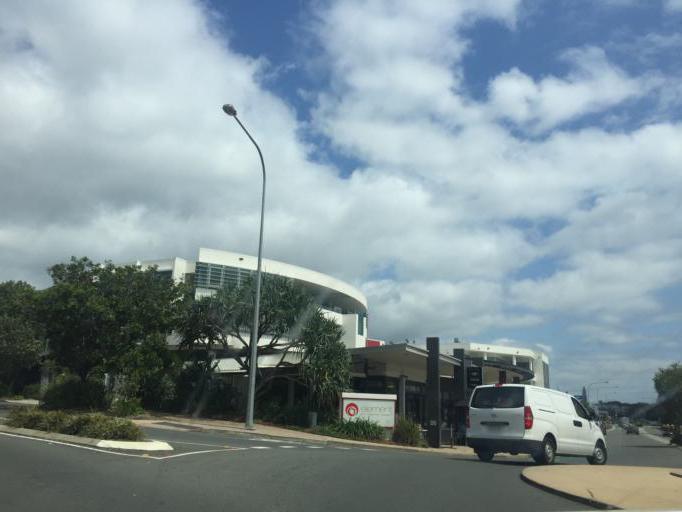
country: AU
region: Queensland
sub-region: Sunshine Coast
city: Coolum Beach
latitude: -26.5293
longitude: 153.0909
